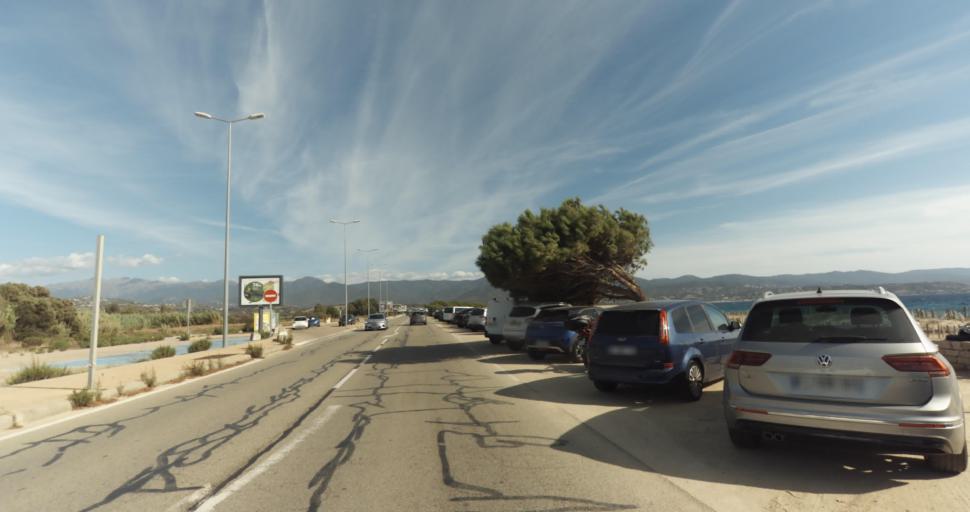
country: FR
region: Corsica
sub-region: Departement de la Corse-du-Sud
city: Ajaccio
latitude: 41.9257
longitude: 8.7798
